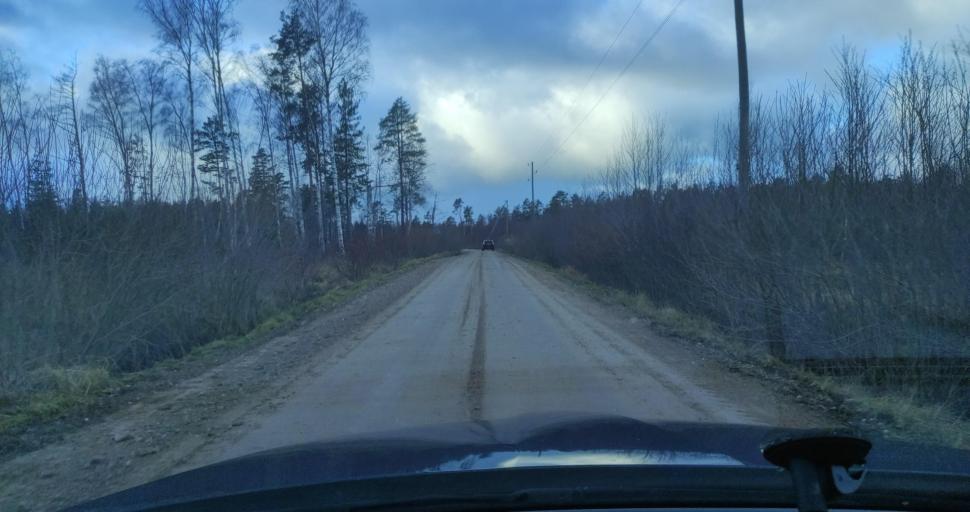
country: LV
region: Pavilostas
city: Pavilosta
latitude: 56.8586
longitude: 21.1658
